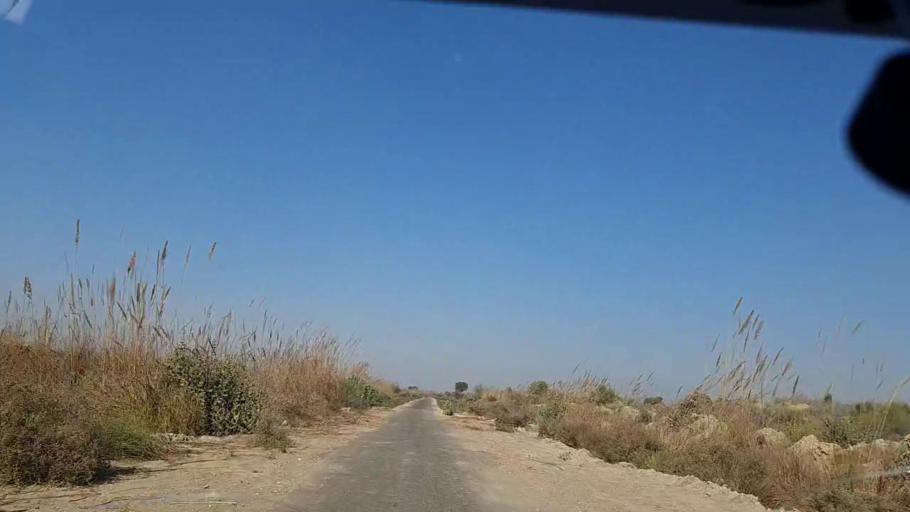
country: PK
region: Sindh
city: Khanpur
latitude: 27.5875
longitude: 69.3758
